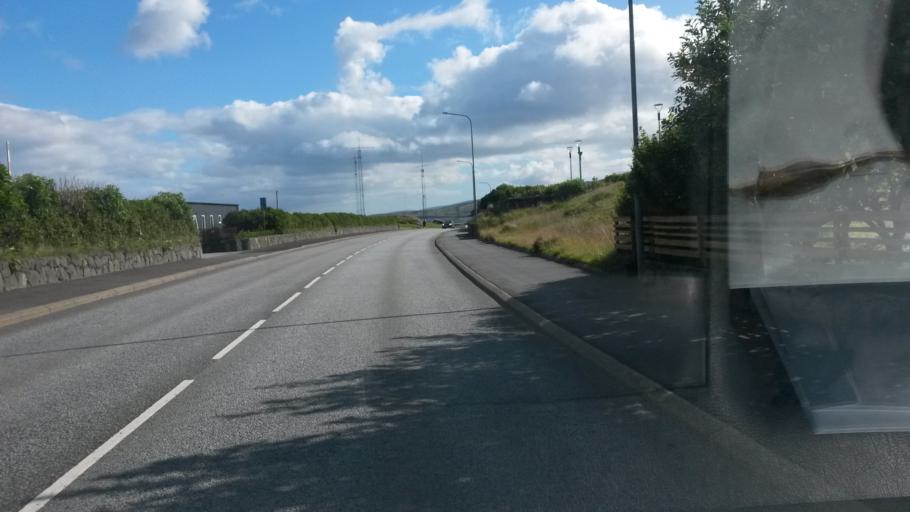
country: FO
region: Streymoy
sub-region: Torshavn
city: Torshavn
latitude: 62.0174
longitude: -6.7557
